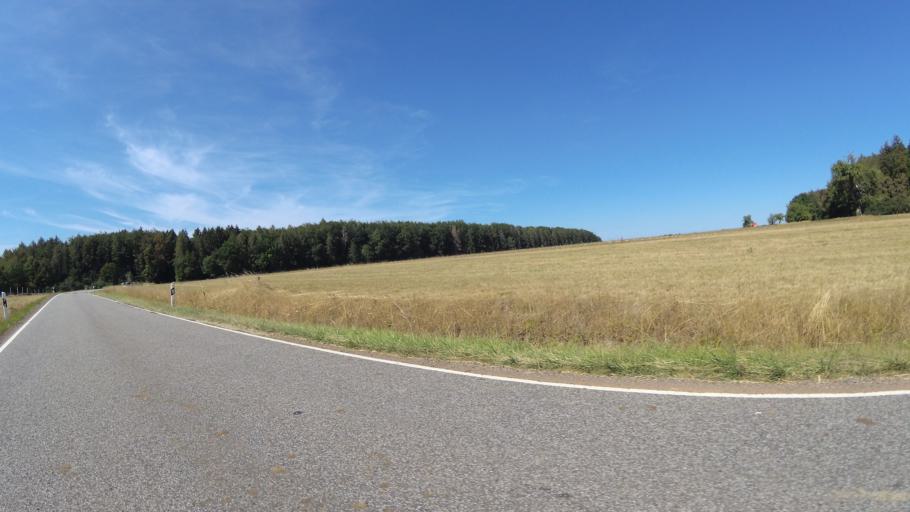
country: DE
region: Rheinland-Pfalz
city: Hornbach
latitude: 49.1595
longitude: 7.3213
